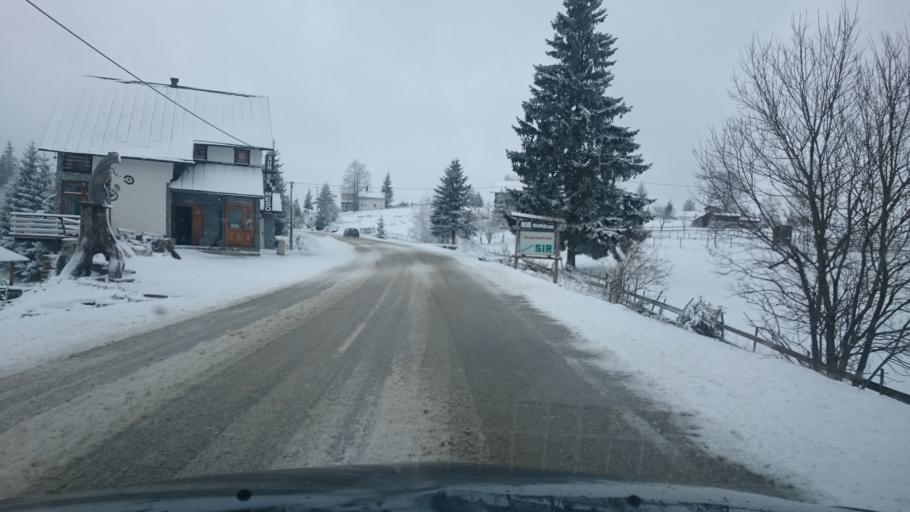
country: BA
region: Federation of Bosnia and Herzegovina
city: Turbe
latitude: 44.3002
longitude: 17.4977
